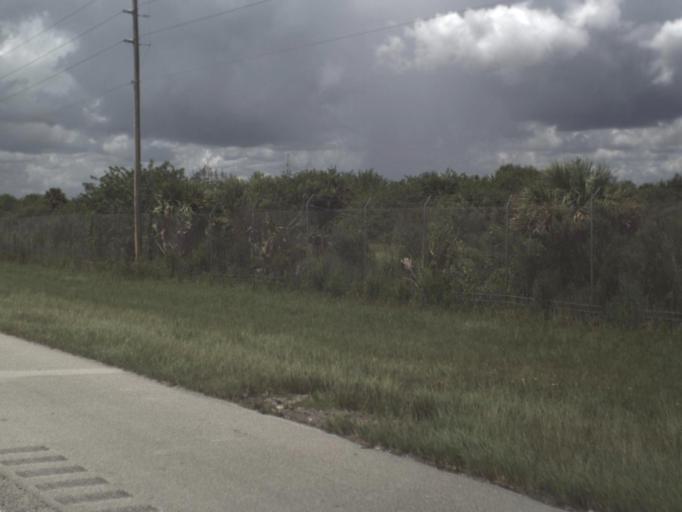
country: US
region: Florida
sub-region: Collier County
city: Immokalee
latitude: 26.1550
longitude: -81.3372
